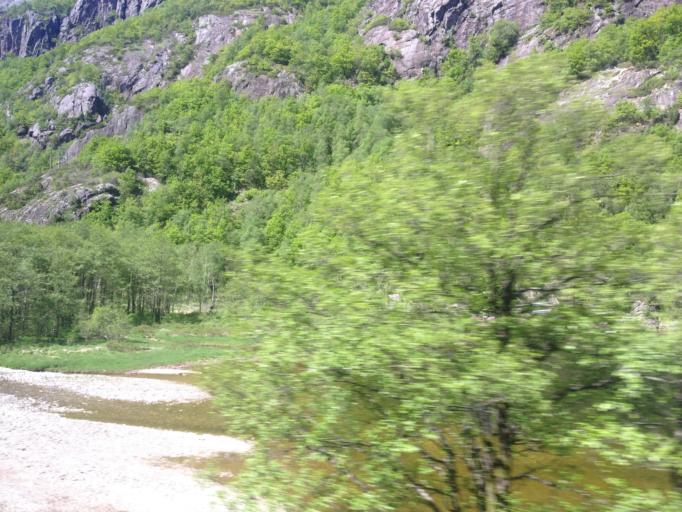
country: NO
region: Rogaland
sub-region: Lund
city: Moi
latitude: 58.4791
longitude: 6.4465
